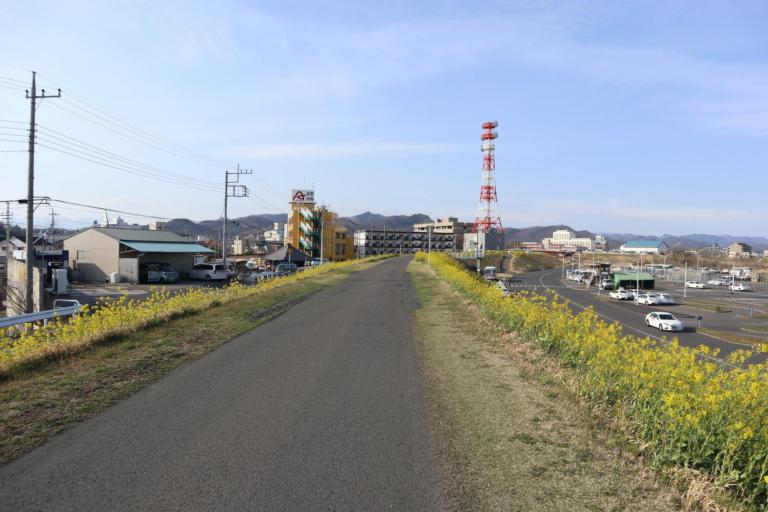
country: JP
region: Tochigi
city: Ashikaga
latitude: 36.3241
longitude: 139.4536
